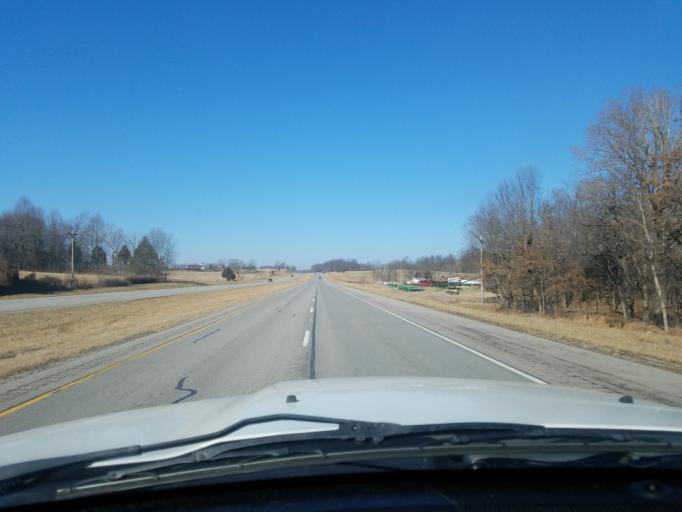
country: US
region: Kentucky
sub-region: Hardin County
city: Elizabethtown
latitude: 37.6230
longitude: -85.8141
